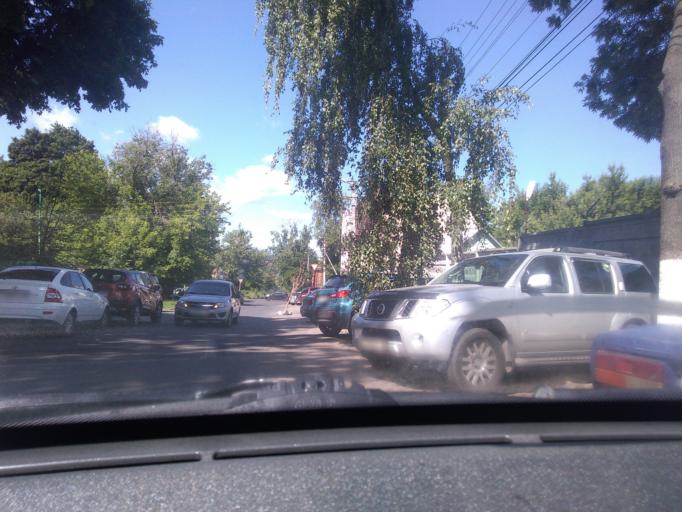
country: RU
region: Kursk
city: Kursk
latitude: 51.7363
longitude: 36.1884
